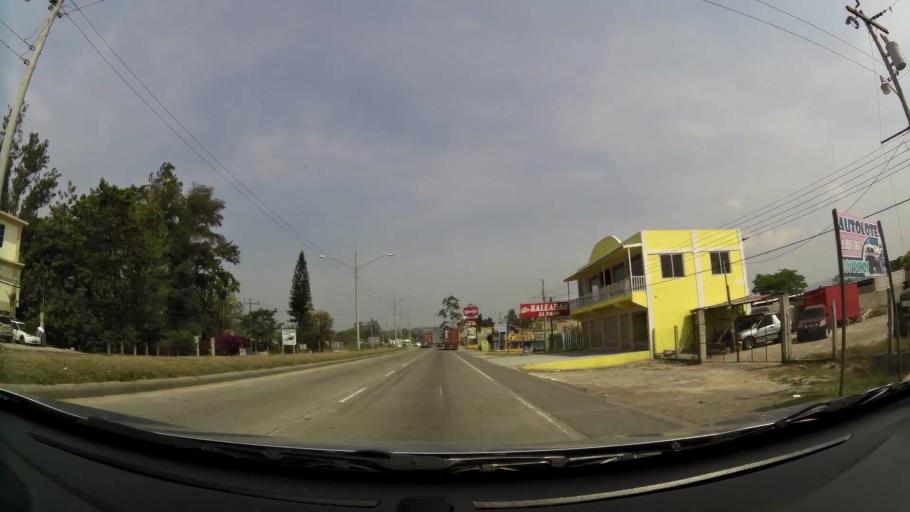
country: HN
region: Comayagua
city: Siguatepeque
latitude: 14.5824
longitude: -87.8446
